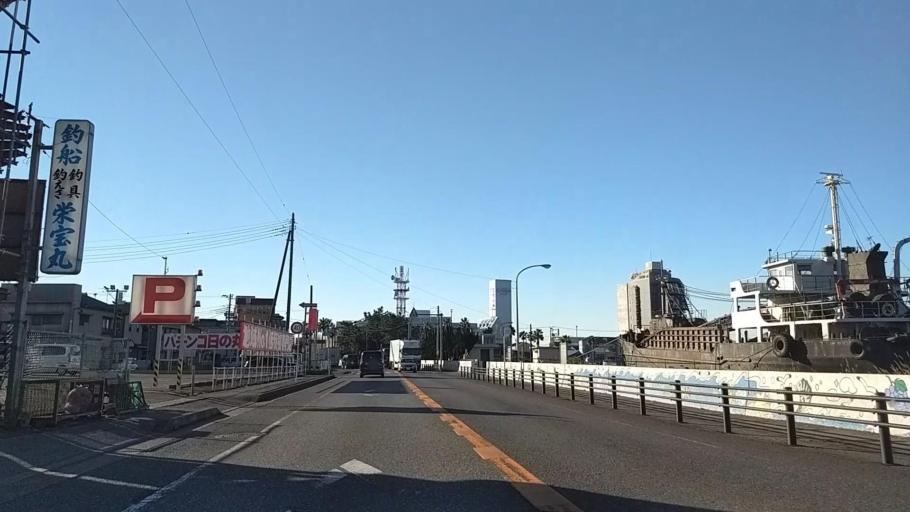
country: JP
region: Chiba
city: Kisarazu
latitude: 35.3834
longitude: 139.9180
